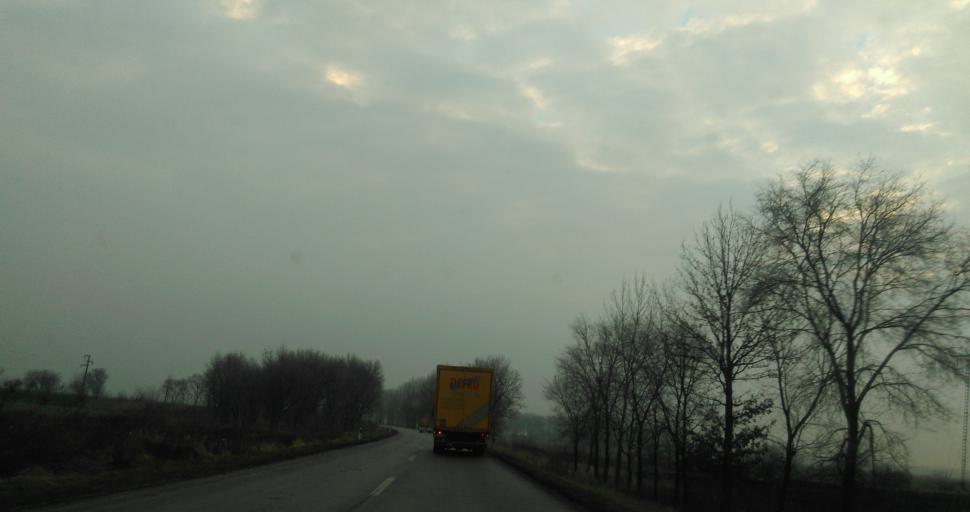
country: RS
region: Autonomna Pokrajina Vojvodina
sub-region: Juznobacki Okrug
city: Becej
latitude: 45.5817
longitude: 20.0761
